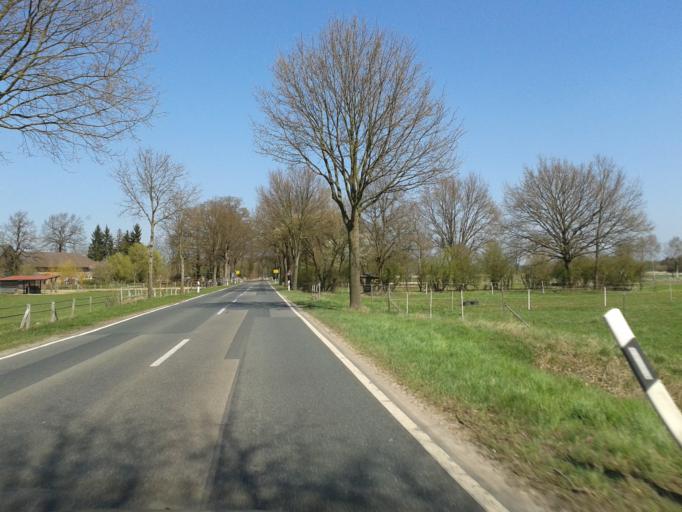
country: DE
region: Lower Saxony
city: Wustrow
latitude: 52.9332
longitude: 11.1166
